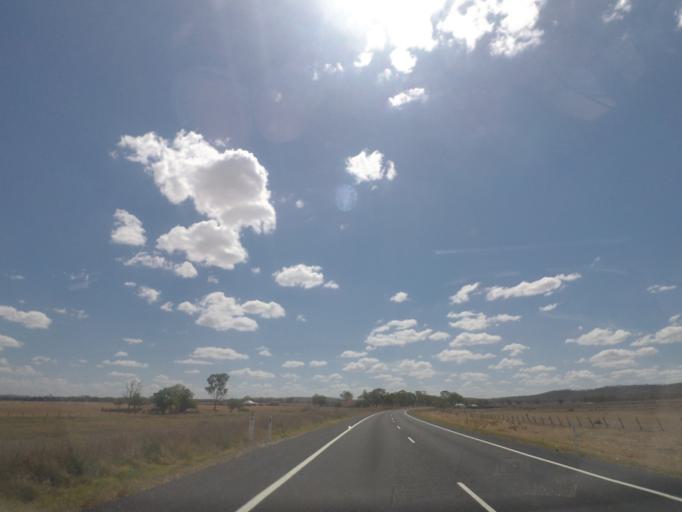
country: AU
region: Queensland
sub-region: Southern Downs
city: Warwick
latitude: -28.1783
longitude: 151.7758
